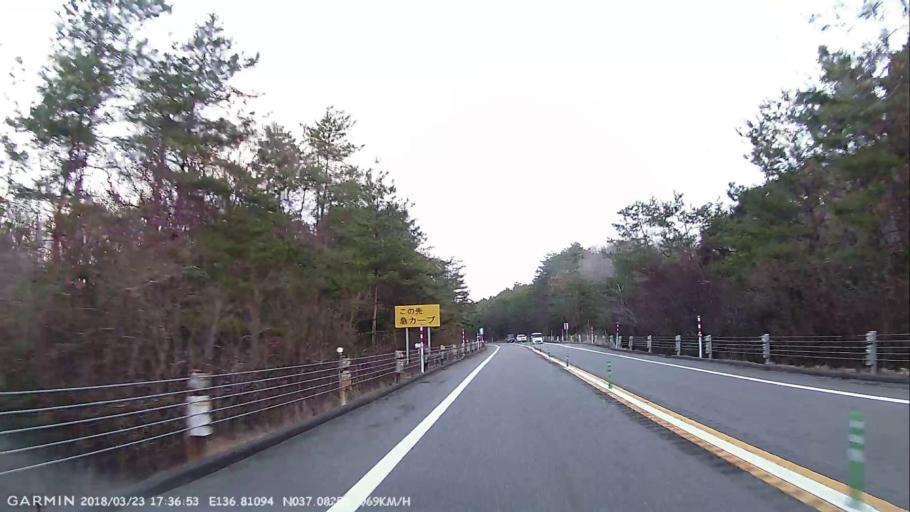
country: JP
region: Ishikawa
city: Nanao
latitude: 37.0827
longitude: 136.8109
